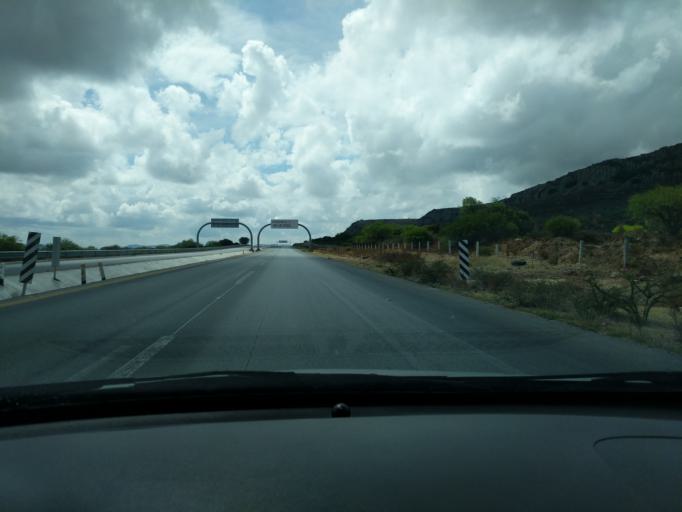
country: MX
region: Zacatecas
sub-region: Pinos
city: Santiago
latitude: 22.4011
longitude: -101.3780
